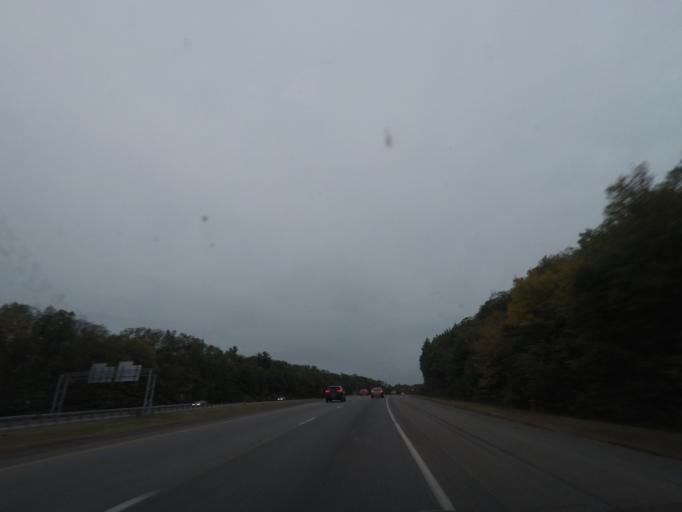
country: US
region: Massachusetts
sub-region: Worcester County
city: Oxford
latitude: 42.1264
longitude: -71.8573
